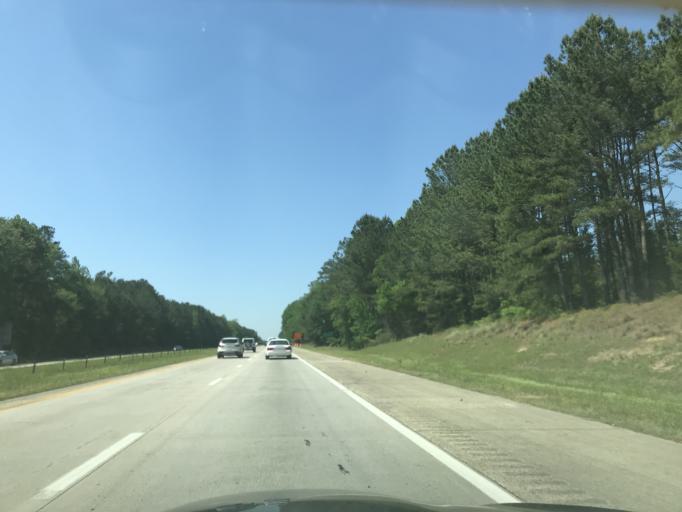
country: US
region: North Carolina
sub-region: Johnston County
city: Benson
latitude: 35.5252
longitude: -78.5638
